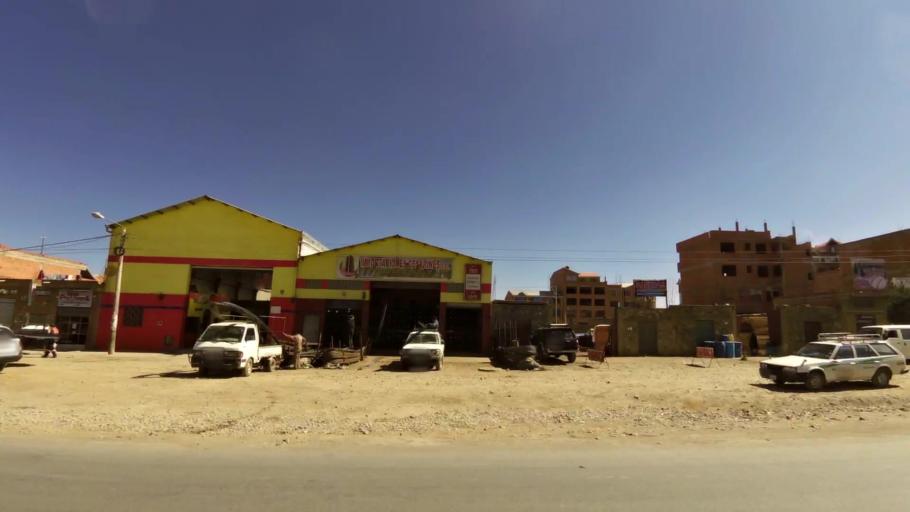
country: BO
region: La Paz
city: La Paz
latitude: -16.5403
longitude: -68.1960
